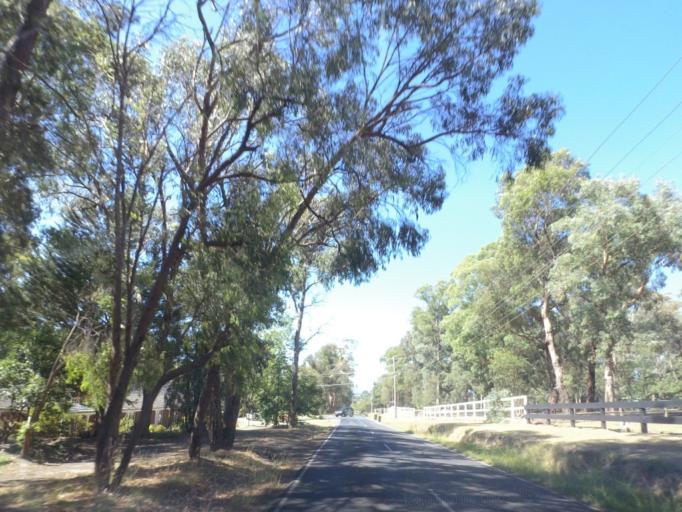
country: AU
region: Victoria
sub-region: Maroondah
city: Croydon Hills
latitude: -37.7426
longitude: 145.2774
